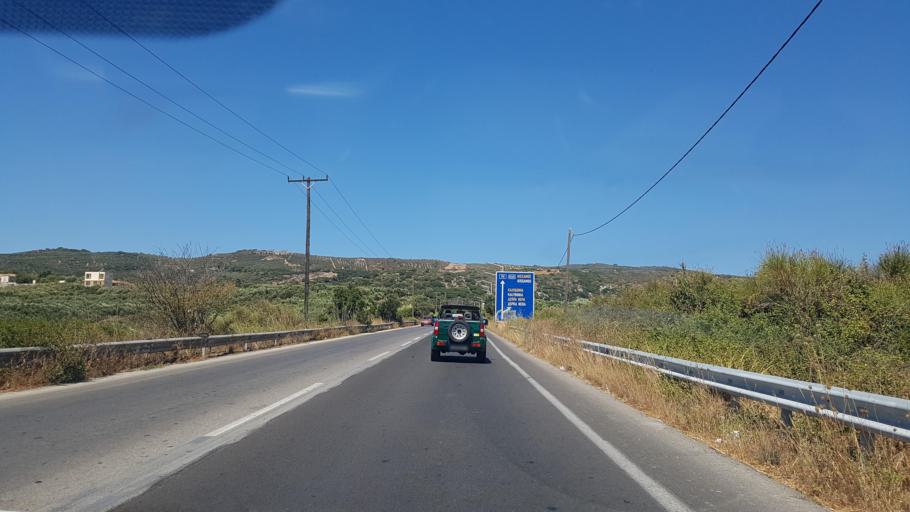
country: GR
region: Crete
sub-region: Nomos Chanias
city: Kolympari
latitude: 35.5281
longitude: 23.7558
